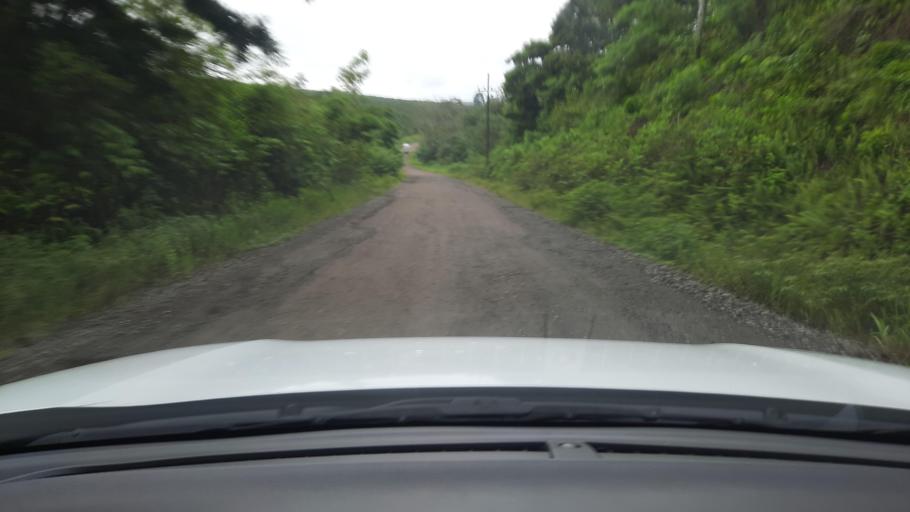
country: CR
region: Alajuela
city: San Jose
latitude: 10.9993
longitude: -85.2853
